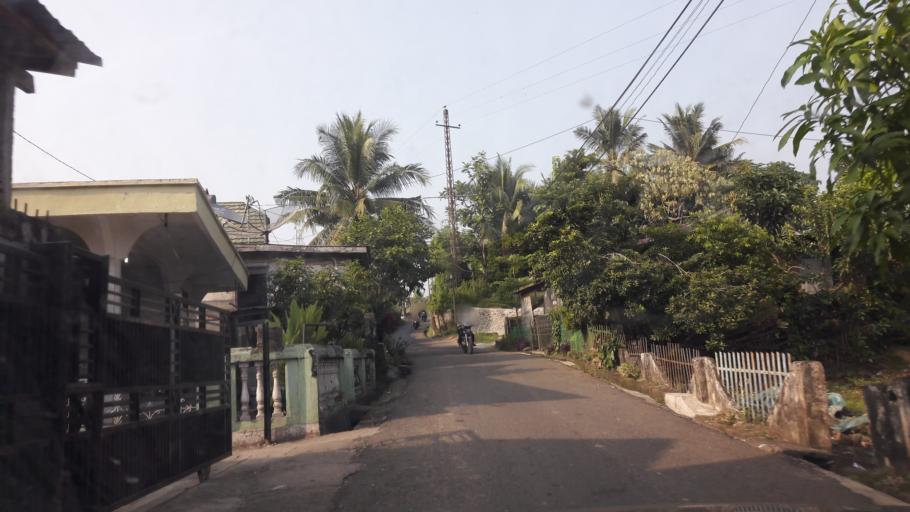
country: ID
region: South Sumatra
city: Gunungmegang Dalam
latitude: -3.2744
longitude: 103.8253
